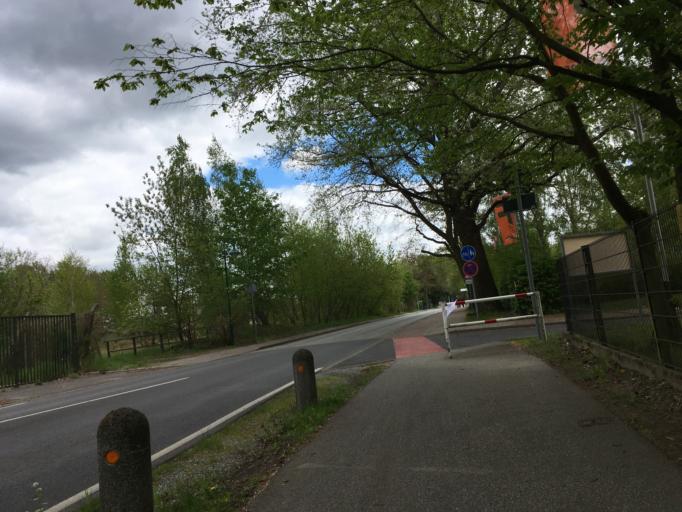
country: DE
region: Berlin
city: Buch
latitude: 52.6555
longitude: 13.5076
